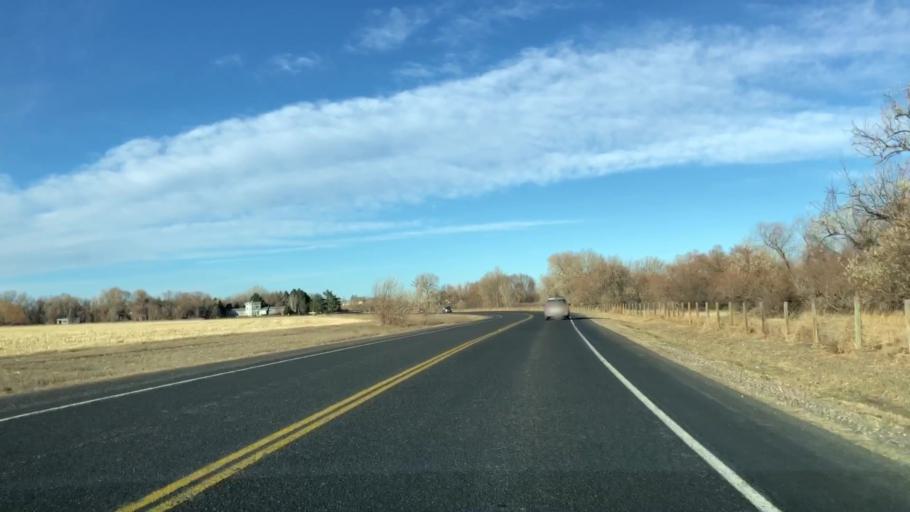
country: US
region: Colorado
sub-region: Weld County
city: Windsor
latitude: 40.5170
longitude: -104.9824
